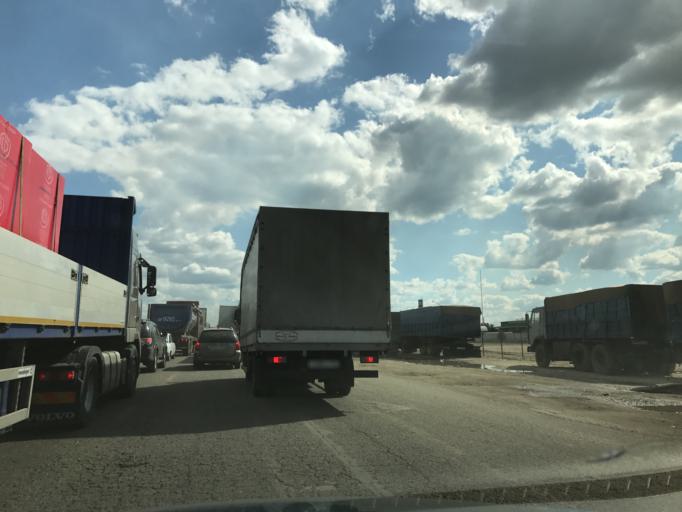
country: RU
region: Adygeya
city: Tlyustenkhabl'
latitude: 44.9542
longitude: 39.1222
